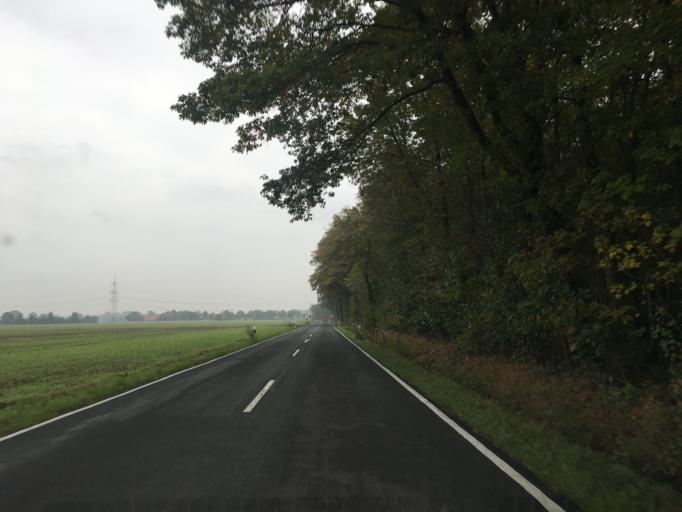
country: DE
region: North Rhine-Westphalia
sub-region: Regierungsbezirk Munster
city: Havixbeck
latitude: 51.9932
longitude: 7.4231
